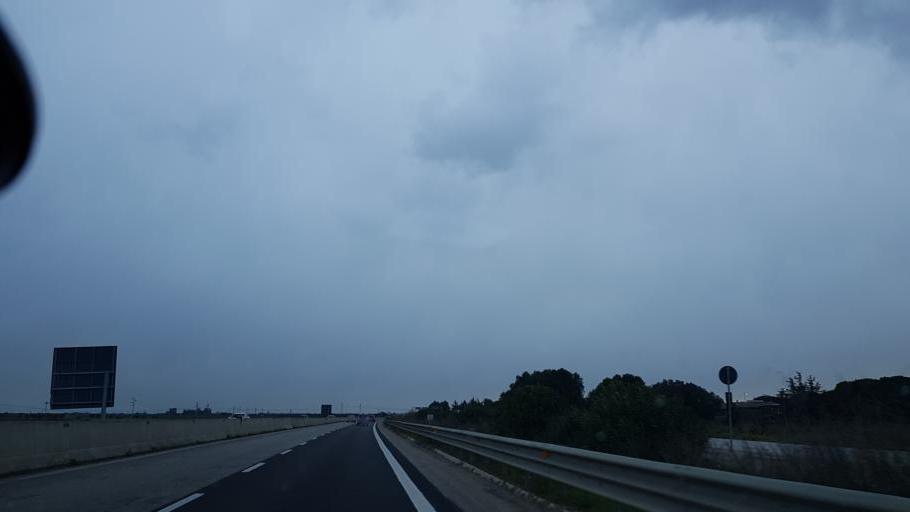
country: IT
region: Apulia
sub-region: Provincia di Brindisi
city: Mesagne
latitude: 40.5881
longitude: 17.8549
